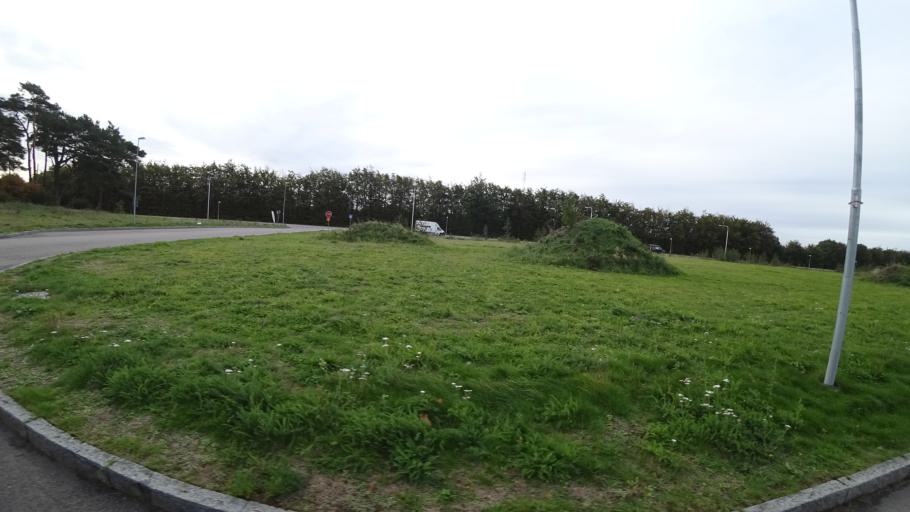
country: SE
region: Skane
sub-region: Kavlinge Kommun
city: Loddekopinge
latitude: 55.7670
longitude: 13.0074
